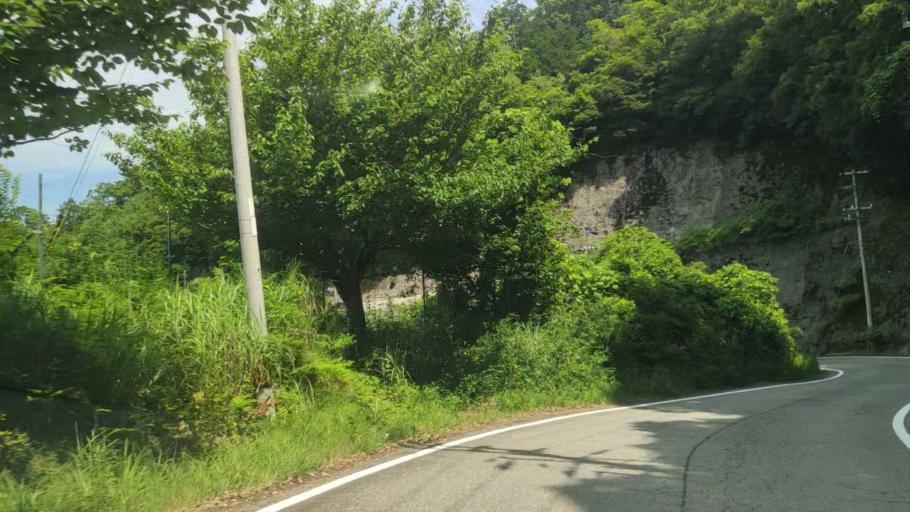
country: JP
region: Hyogo
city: Toyooka
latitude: 35.6418
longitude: 134.7646
